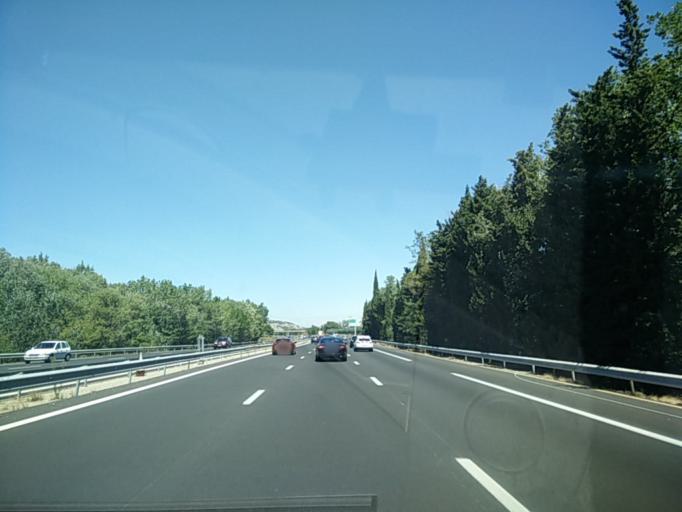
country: FR
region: Provence-Alpes-Cote d'Azur
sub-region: Departement des Bouches-du-Rhone
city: Orgon
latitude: 43.7993
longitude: 5.0400
